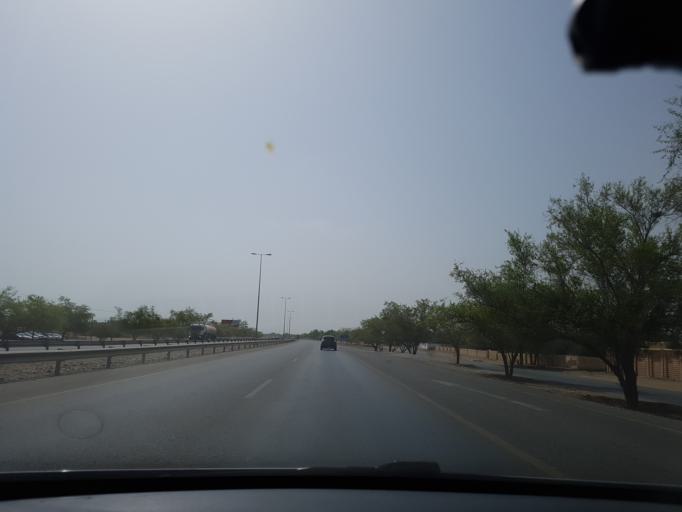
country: OM
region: Al Batinah
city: Al Khaburah
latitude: 23.9467
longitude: 57.1130
